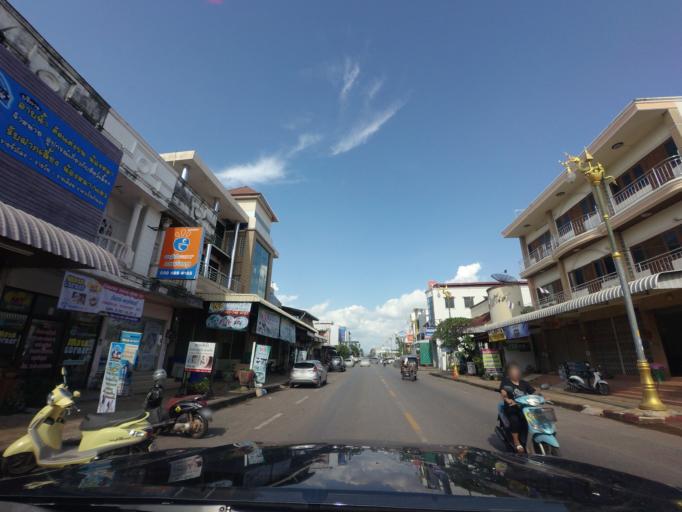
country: TH
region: Nong Khai
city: Nong Khai
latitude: 17.8799
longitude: 102.7432
